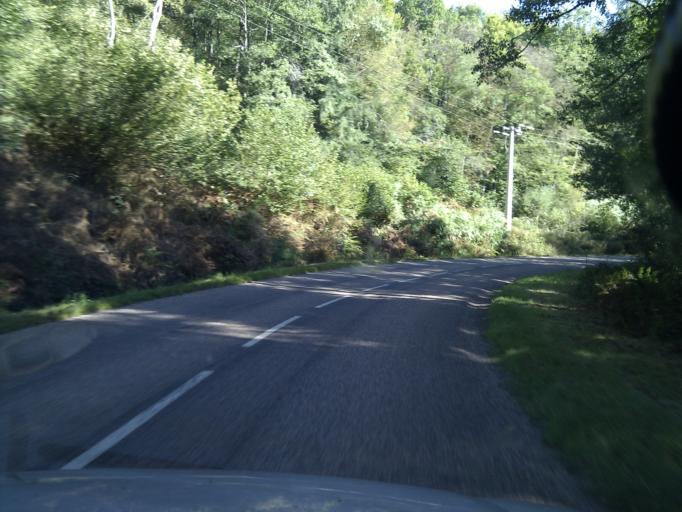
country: FR
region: Bourgogne
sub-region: Departement de la Cote-d'Or
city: Saulieu
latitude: 47.2817
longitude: 4.0644
